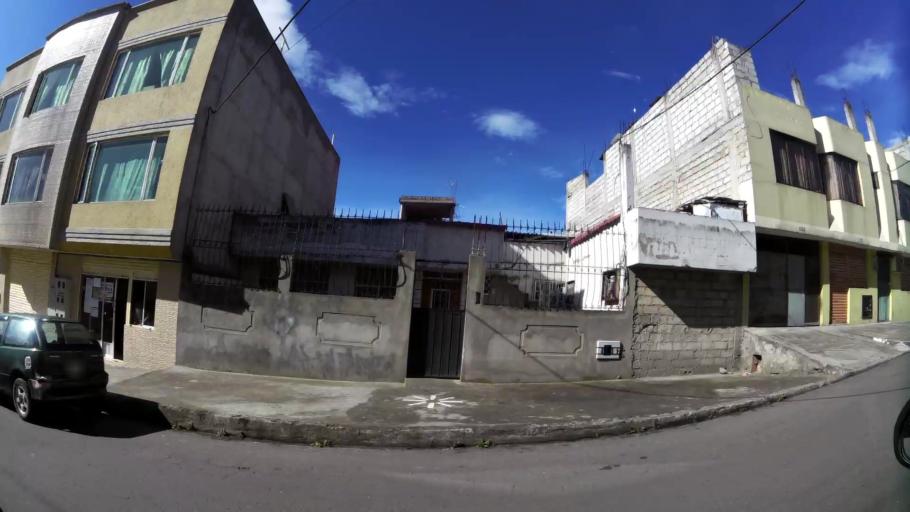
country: EC
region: Pichincha
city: Quito
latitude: -0.3042
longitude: -78.5650
